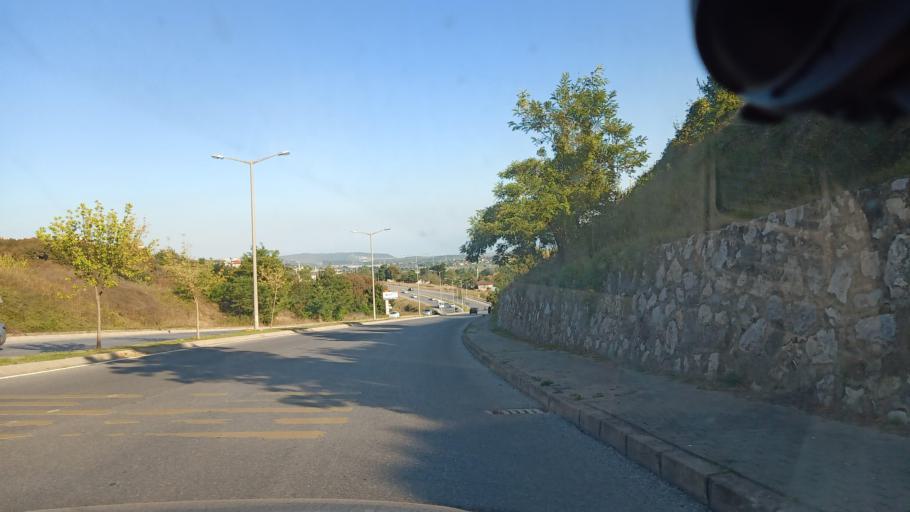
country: TR
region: Sakarya
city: Kazimpasa
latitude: 40.8542
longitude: 30.2982
